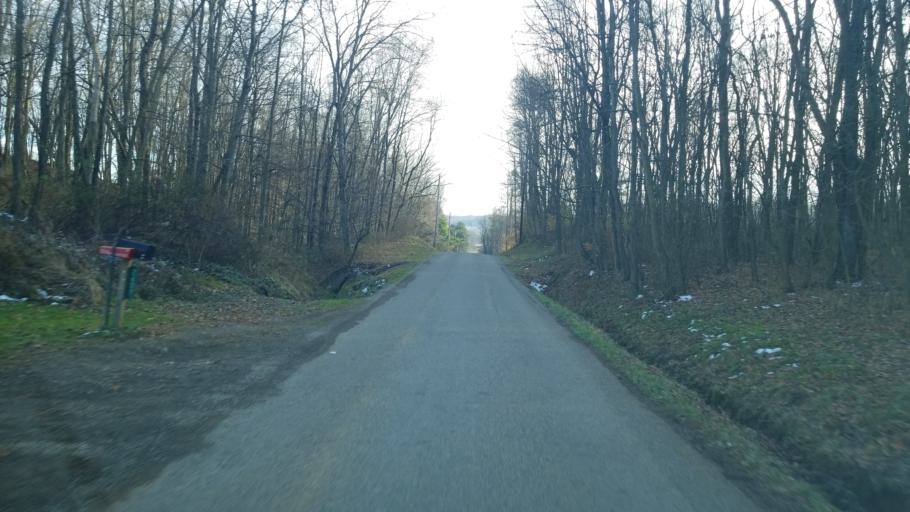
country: US
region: Ohio
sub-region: Ashland County
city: Loudonville
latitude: 40.7116
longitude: -82.3392
